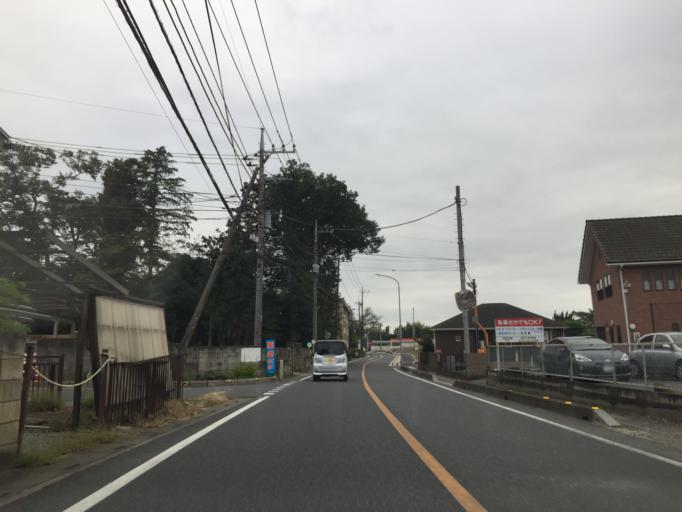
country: JP
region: Saitama
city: Okegawa
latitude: 35.9652
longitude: 139.5576
